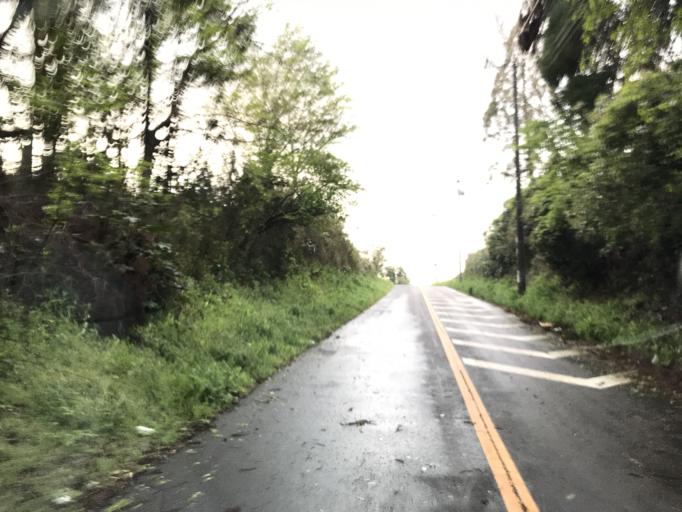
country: JP
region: Chiba
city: Sawara
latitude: 35.7743
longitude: 140.4538
